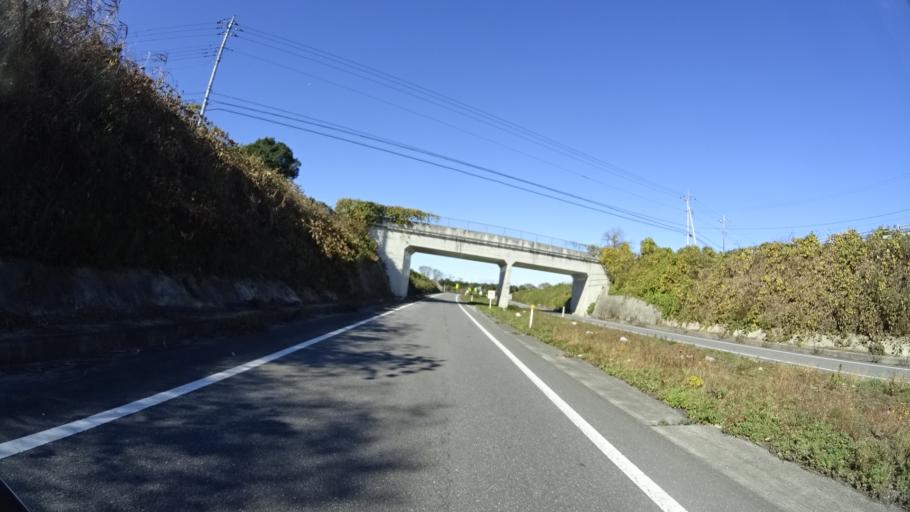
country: JP
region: Tochigi
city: Kanuma
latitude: 36.4924
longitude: 139.7523
